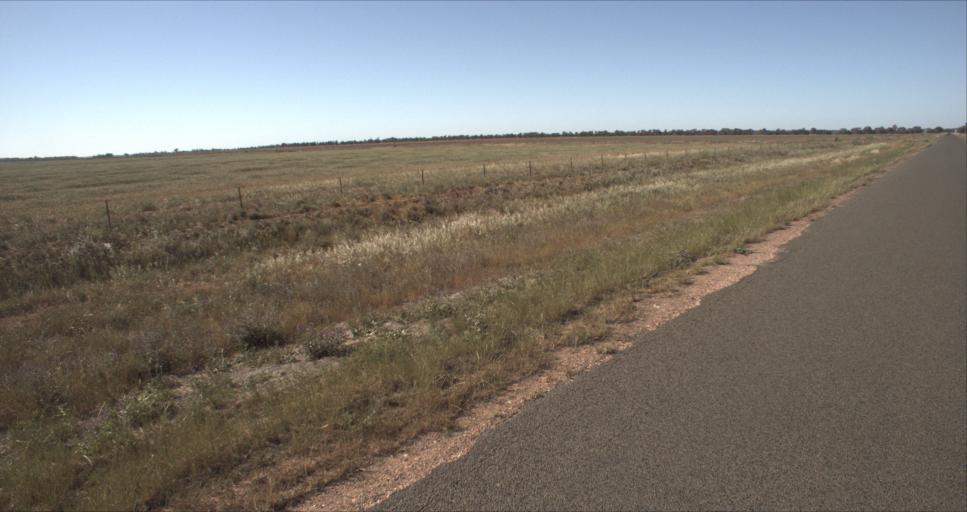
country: AU
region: New South Wales
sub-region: Leeton
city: Leeton
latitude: -34.5654
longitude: 146.2645
